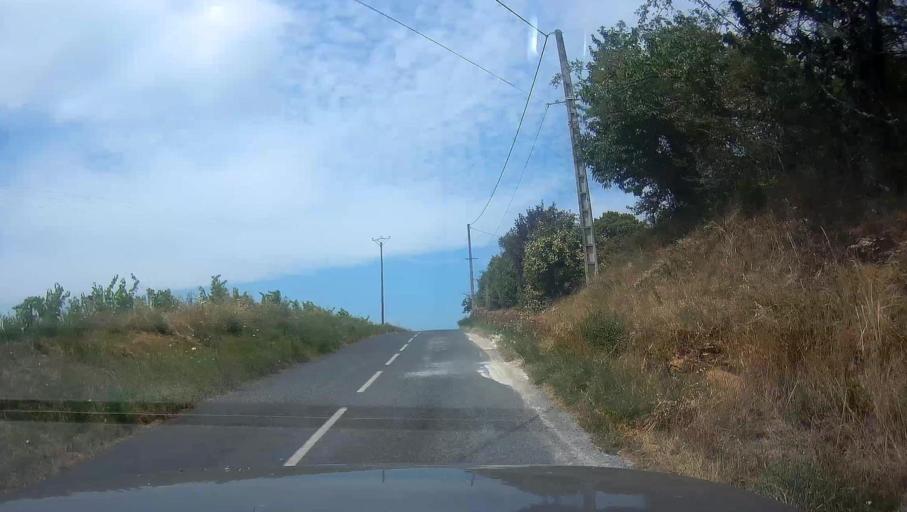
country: FR
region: Rhone-Alpes
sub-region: Departement du Rhone
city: Theize
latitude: 45.9401
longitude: 4.5964
